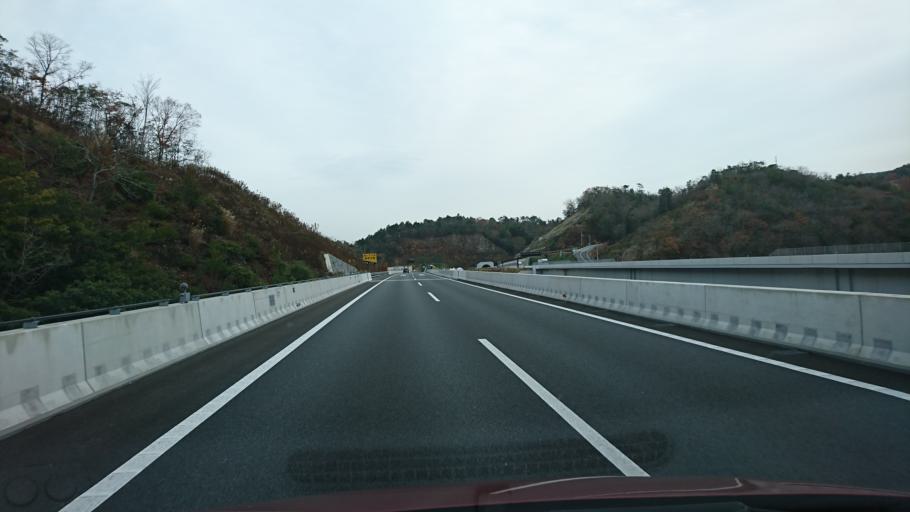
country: JP
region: Hyogo
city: Takarazuka
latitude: 34.8716
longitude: 135.3180
